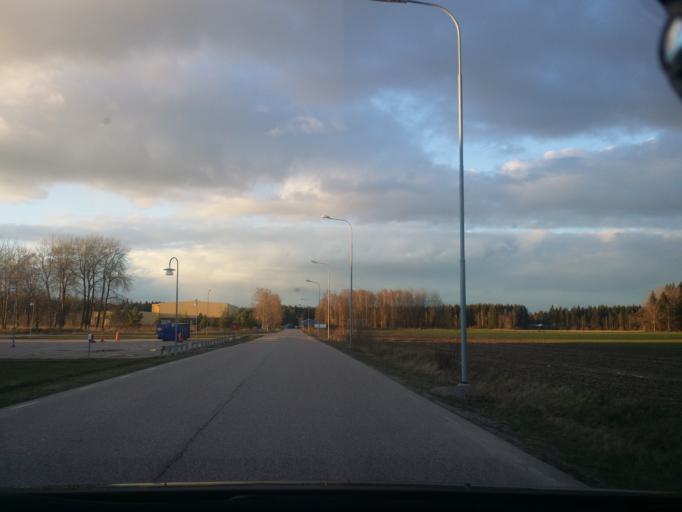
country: SE
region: Vaestmanland
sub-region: Vasteras
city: Hokasen
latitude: 59.6475
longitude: 16.5880
